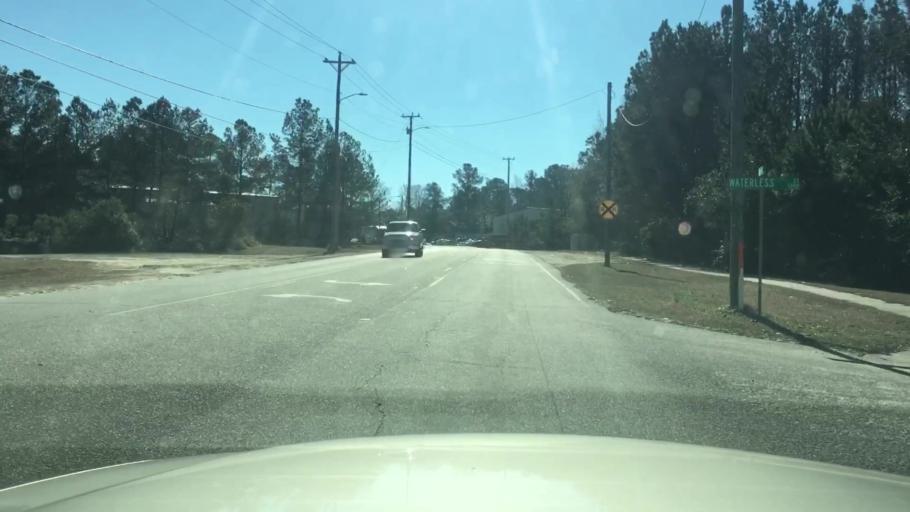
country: US
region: North Carolina
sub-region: Cumberland County
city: Fayetteville
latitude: 35.0391
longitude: -78.8967
